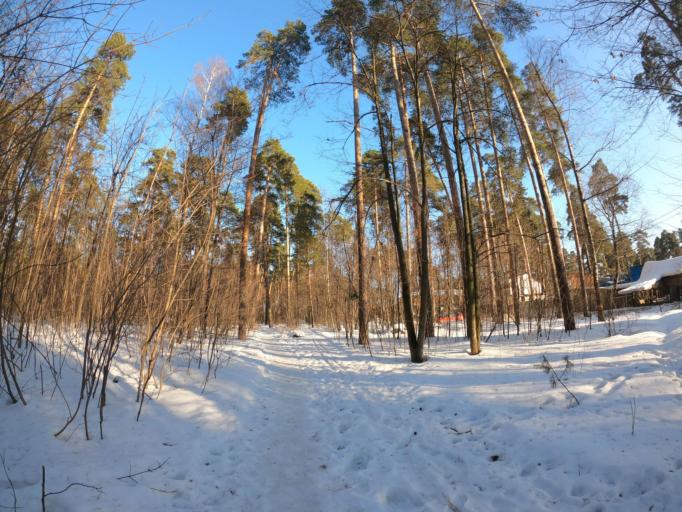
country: RU
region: Moskovskaya
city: Udel'naya
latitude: 55.6372
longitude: 38.0011
